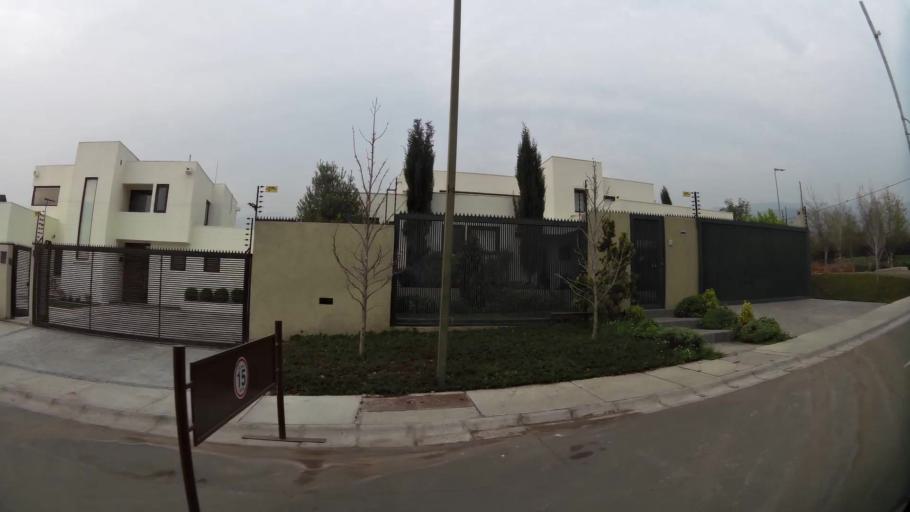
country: CL
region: Santiago Metropolitan
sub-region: Provincia de Chacabuco
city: Chicureo Abajo
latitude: -33.2713
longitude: -70.6228
